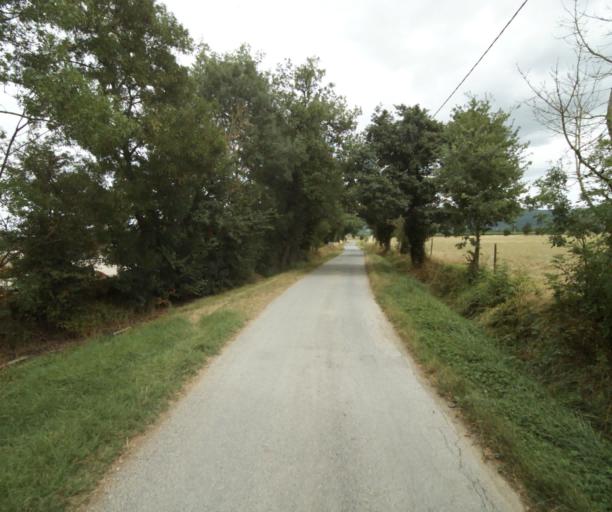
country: FR
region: Midi-Pyrenees
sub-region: Departement du Tarn
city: Soreze
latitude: 43.4778
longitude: 2.0443
